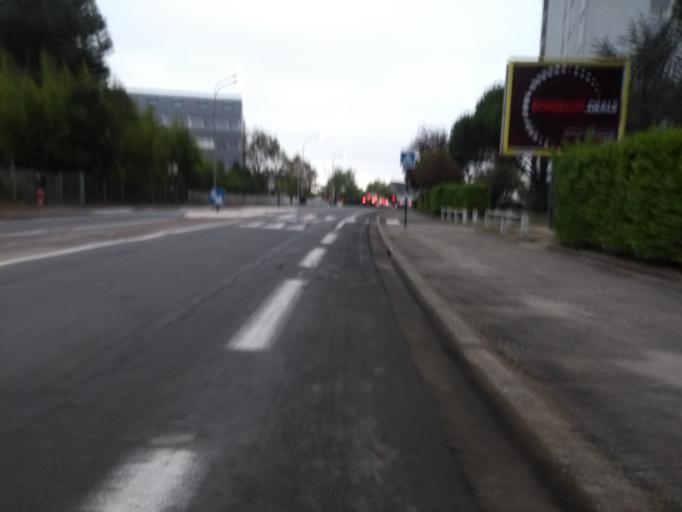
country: FR
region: Aquitaine
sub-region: Departement de la Gironde
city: Talence
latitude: 44.7973
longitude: -0.5989
